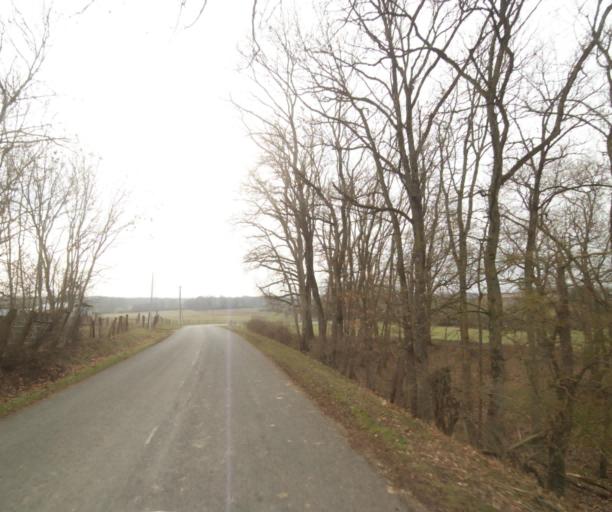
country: FR
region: Champagne-Ardenne
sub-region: Departement de la Marne
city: Pargny-sur-Saulx
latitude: 48.7440
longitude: 4.8420
